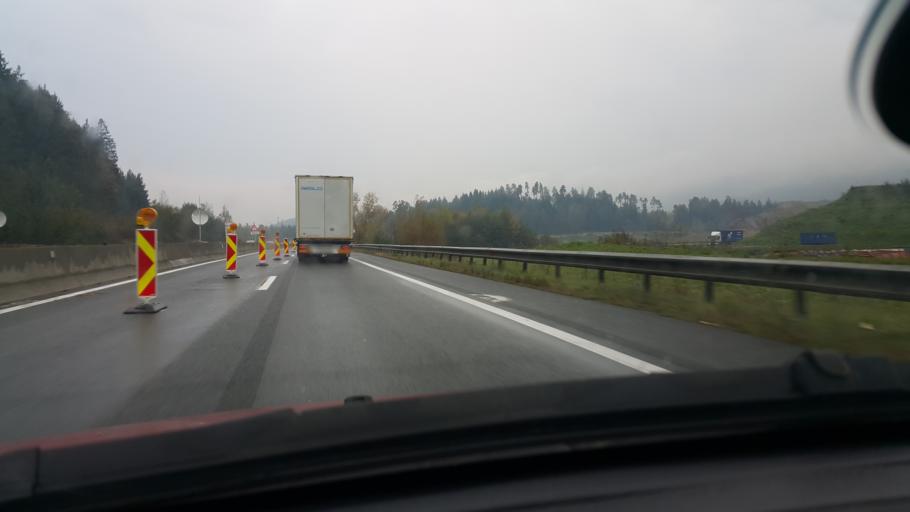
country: AT
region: Carinthia
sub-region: Politischer Bezirk Volkermarkt
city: Voelkermarkt
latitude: 46.6467
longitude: 14.5460
